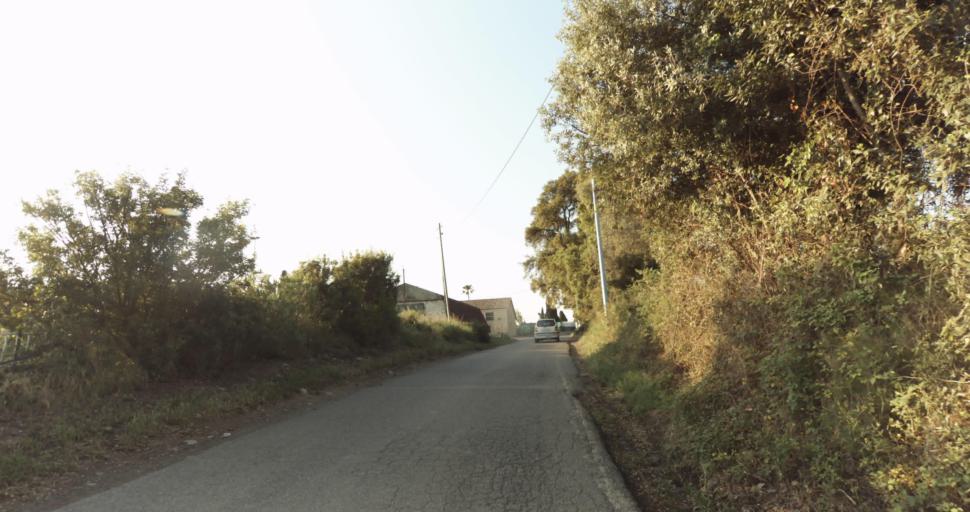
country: FR
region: Corsica
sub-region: Departement de la Haute-Corse
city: Biguglia
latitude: 42.6096
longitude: 9.4434
